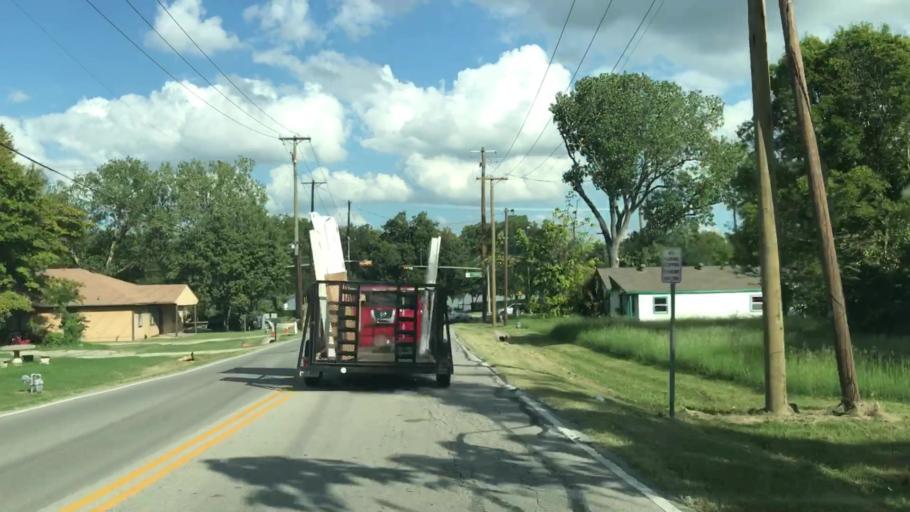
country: US
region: Texas
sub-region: Dallas County
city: Rowlett
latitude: 32.8810
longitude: -96.5193
